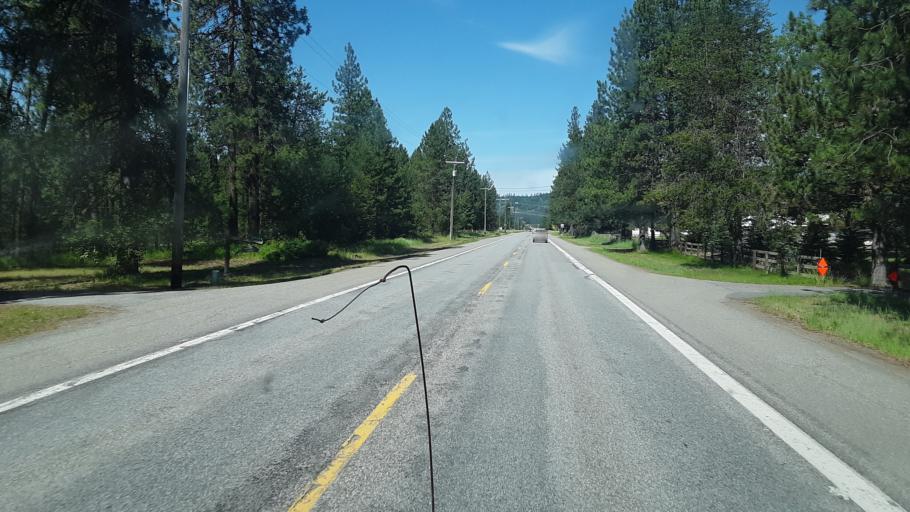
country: US
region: Idaho
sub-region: Kootenai County
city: Rathdrum
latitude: 47.8172
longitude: -116.8468
